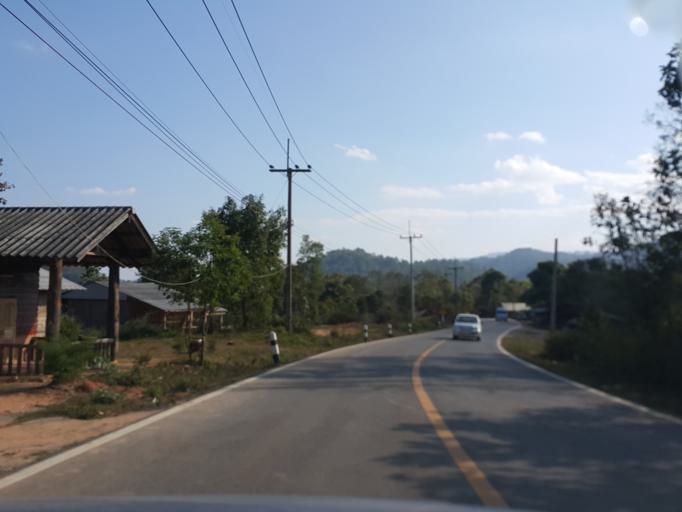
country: TH
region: Chiang Mai
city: Mae Wang
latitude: 18.6910
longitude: 98.5664
